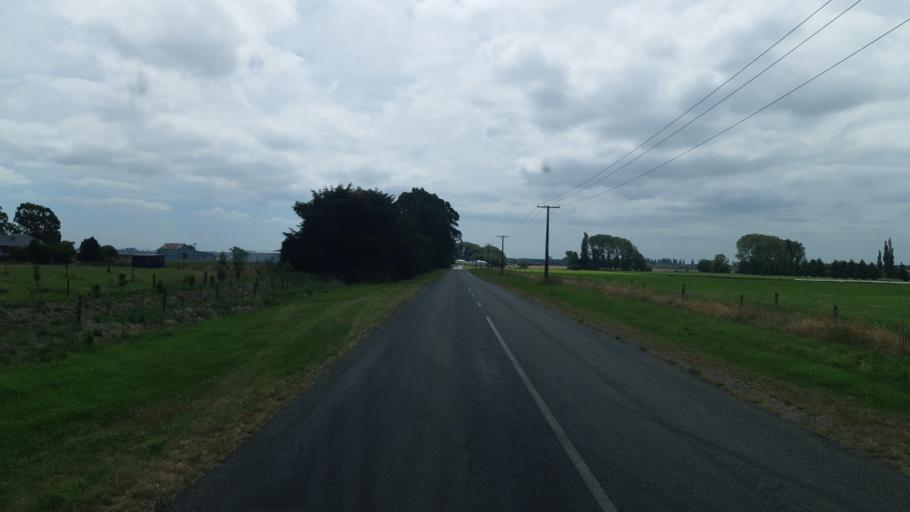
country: NZ
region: Canterbury
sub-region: Timaru District
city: Timaru
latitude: -44.2389
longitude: 171.3457
